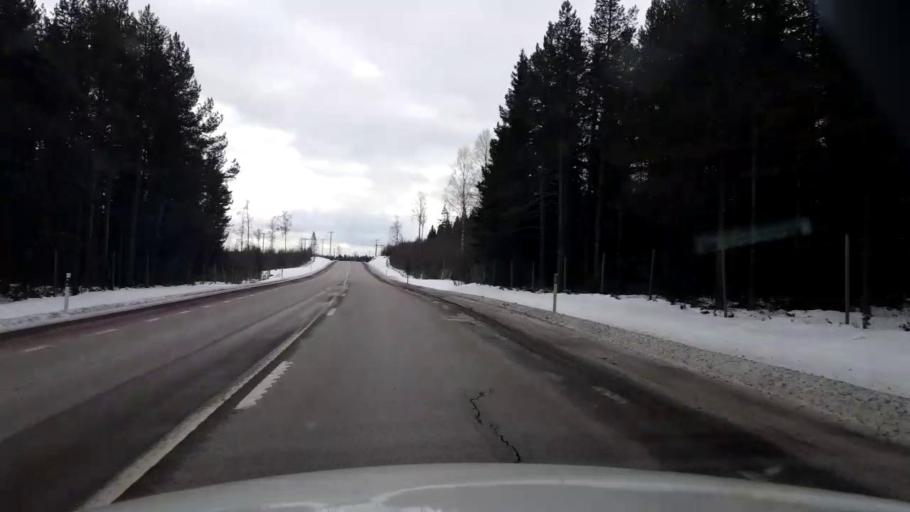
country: SE
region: Gaevleborg
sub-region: Nordanstigs Kommun
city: Bergsjoe
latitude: 62.0045
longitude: 17.2367
